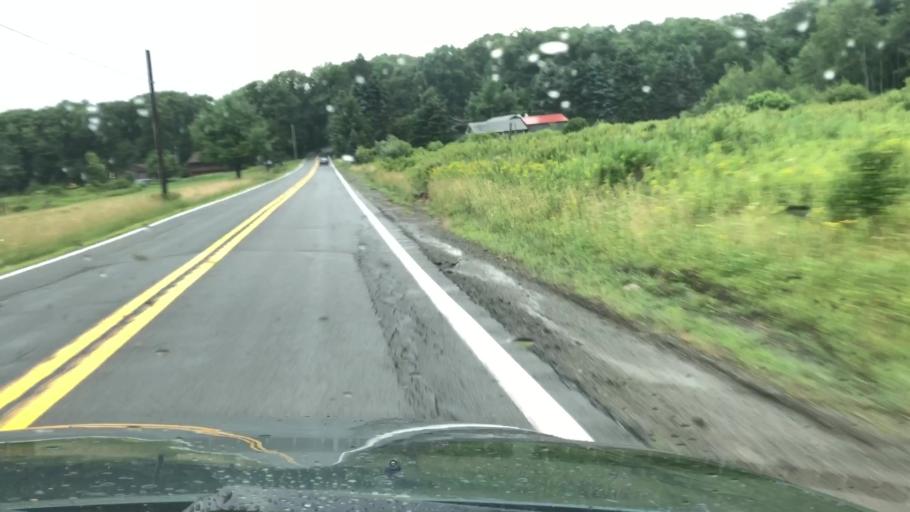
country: US
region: Pennsylvania
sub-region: Monroe County
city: Mountainhome
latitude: 41.2672
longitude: -75.2418
